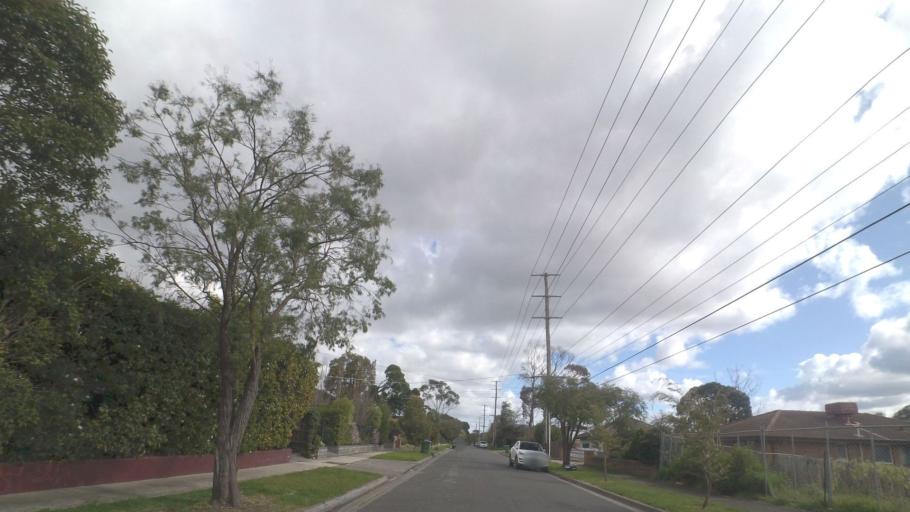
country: AU
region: Victoria
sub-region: Maroondah
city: Ringwood East
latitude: -37.8151
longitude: 145.2361
